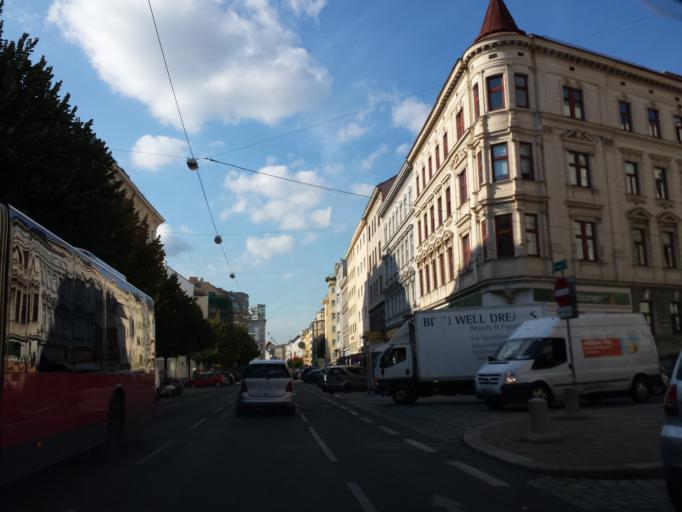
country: AT
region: Vienna
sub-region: Wien Stadt
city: Vienna
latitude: 48.1949
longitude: 16.3971
